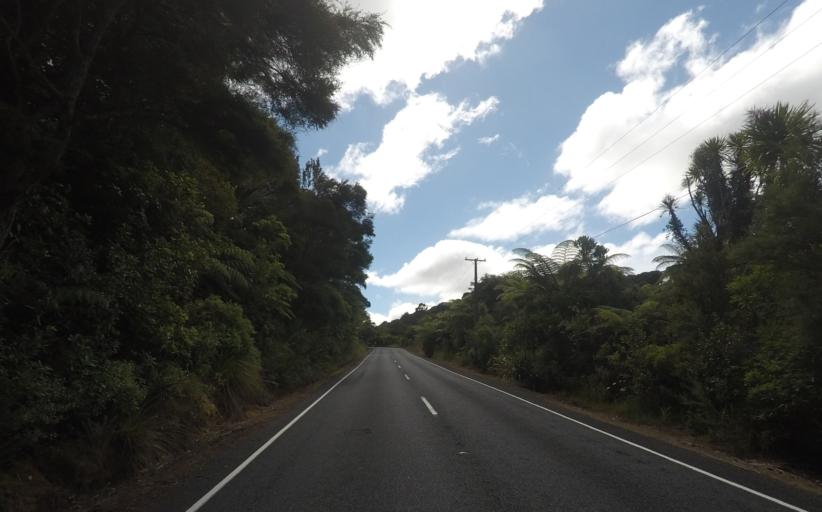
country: NZ
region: Auckland
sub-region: Auckland
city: Muriwai Beach
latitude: -36.8646
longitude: 174.5125
